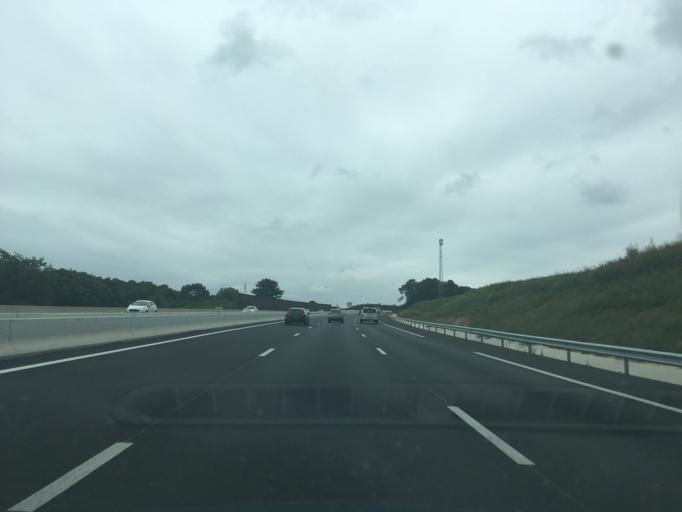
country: FR
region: Aquitaine
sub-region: Departement des Landes
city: Ondres
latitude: 43.5595
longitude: -1.4306
